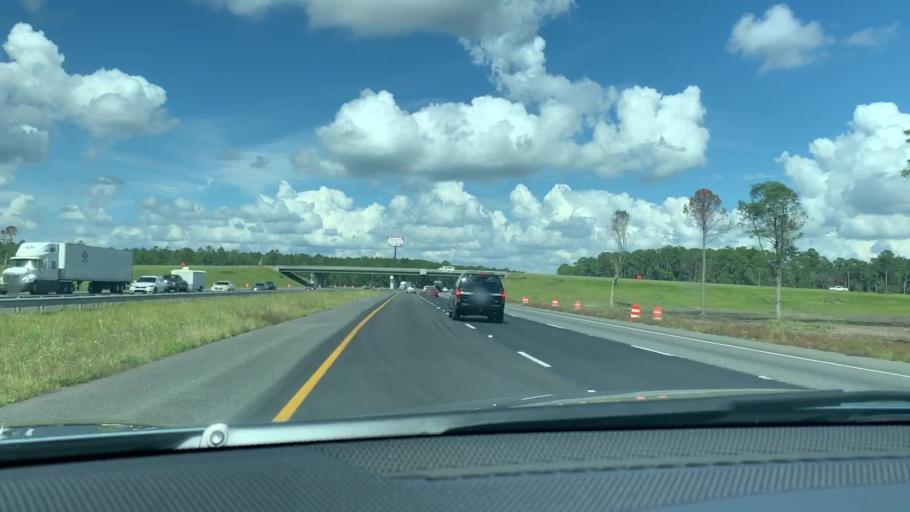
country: US
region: Georgia
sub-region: Camden County
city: Woodbine
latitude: 30.9436
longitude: -81.6863
